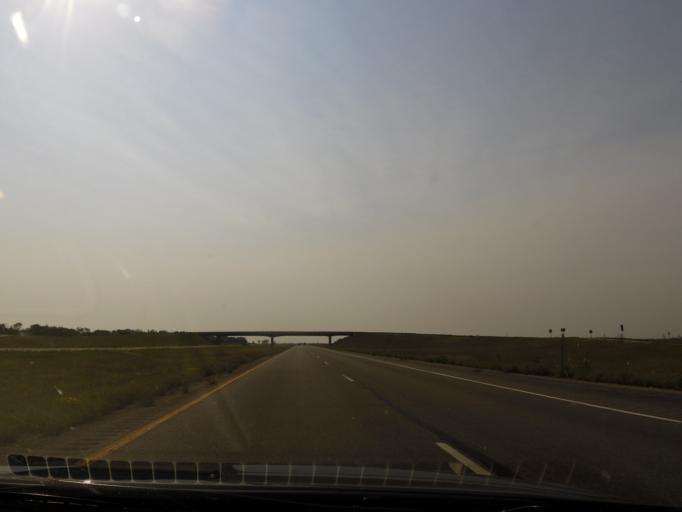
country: US
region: North Dakota
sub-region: Traill County
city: Hillsboro
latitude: 47.2411
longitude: -97.0119
